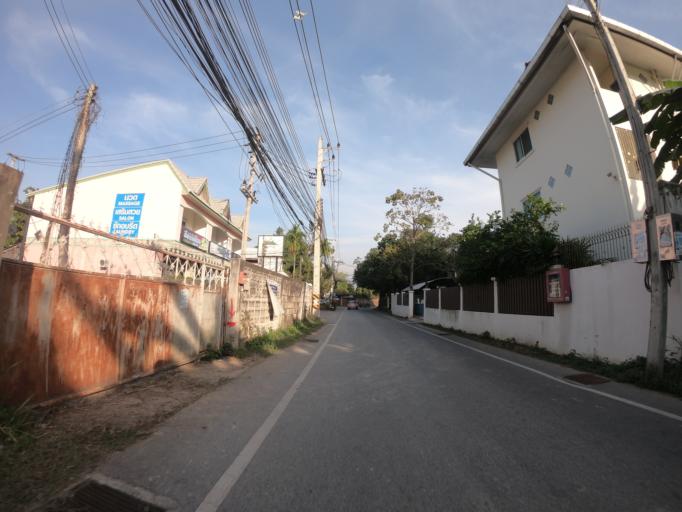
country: TH
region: Chiang Mai
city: Chiang Mai
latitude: 18.8169
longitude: 98.9611
